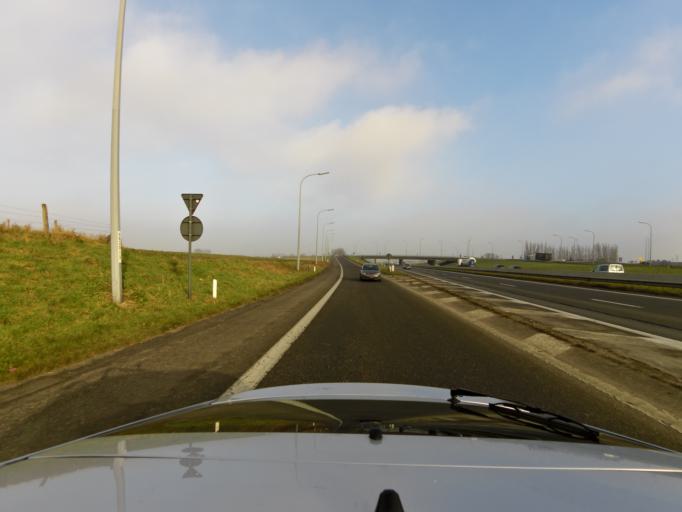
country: BE
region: Flanders
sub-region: Provincie West-Vlaanderen
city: Lichtervelde
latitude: 51.0070
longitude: 3.1713
